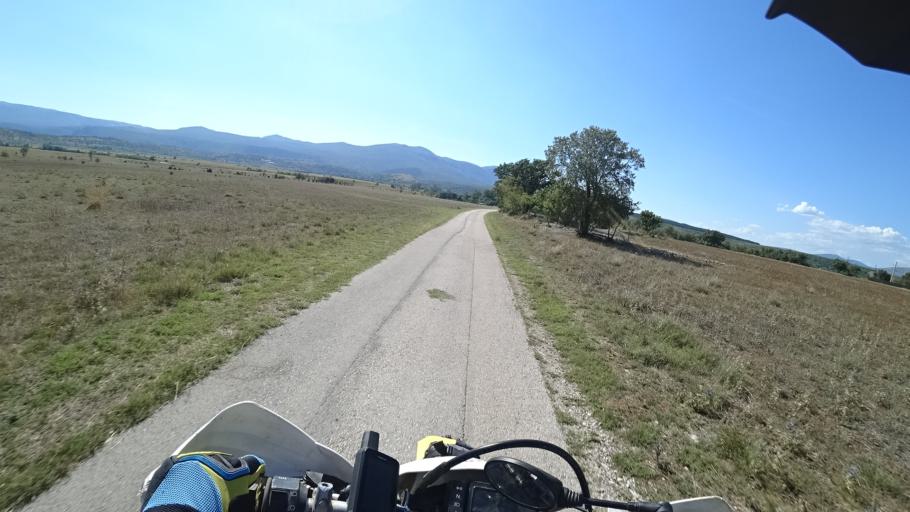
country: BA
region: Federation of Bosnia and Herzegovina
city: Bosansko Grahovo
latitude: 43.9600
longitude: 16.4363
